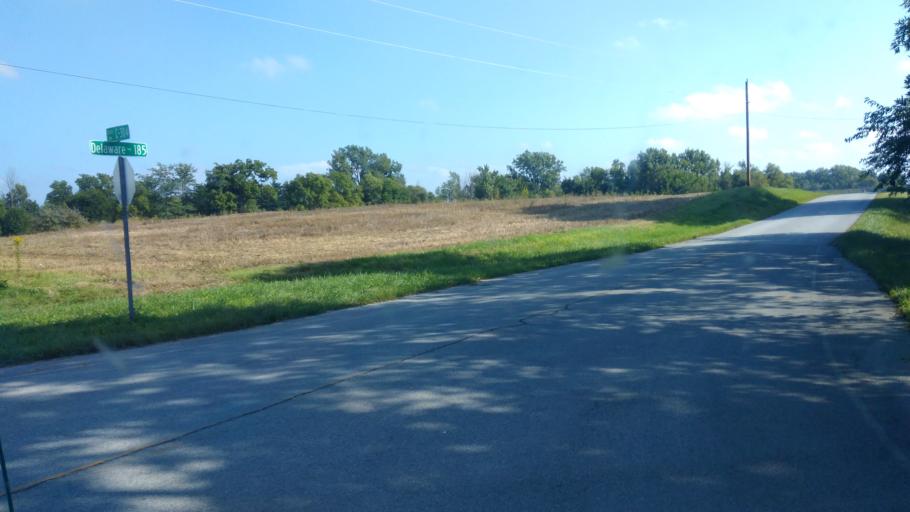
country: US
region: Ohio
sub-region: Hardin County
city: Forest
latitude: 40.8333
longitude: -83.5763
